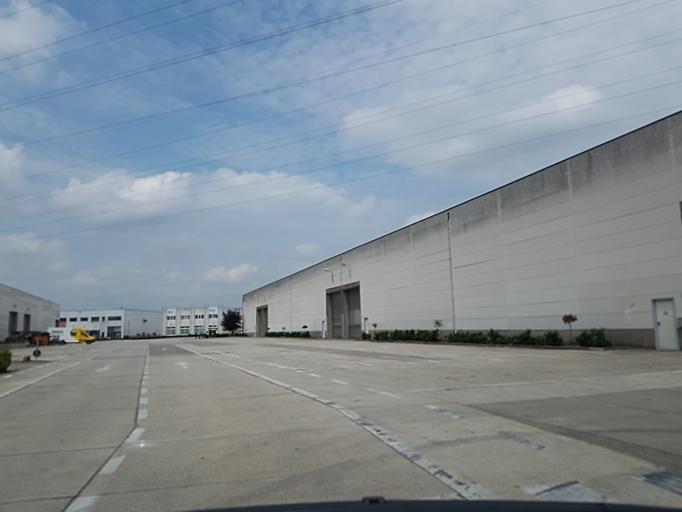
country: BE
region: Flanders
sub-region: Provincie Antwerpen
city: Schoten
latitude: 51.2374
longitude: 4.4828
